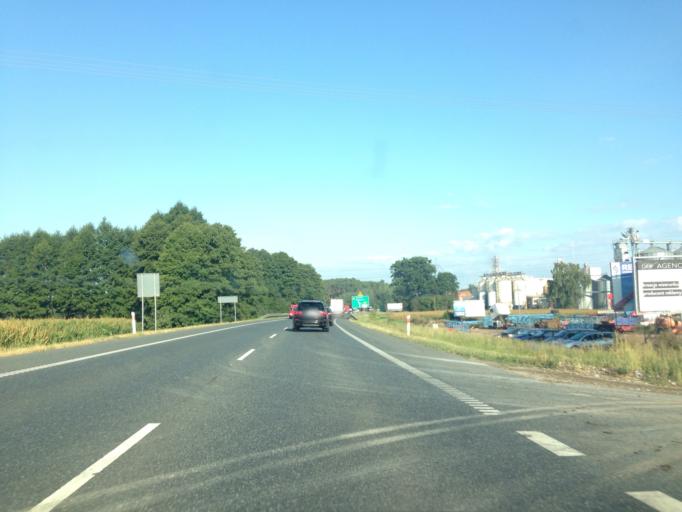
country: PL
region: Kujawsko-Pomorskie
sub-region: Powiat bydgoski
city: Solec Kujawski
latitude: 53.0651
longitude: 18.1673
